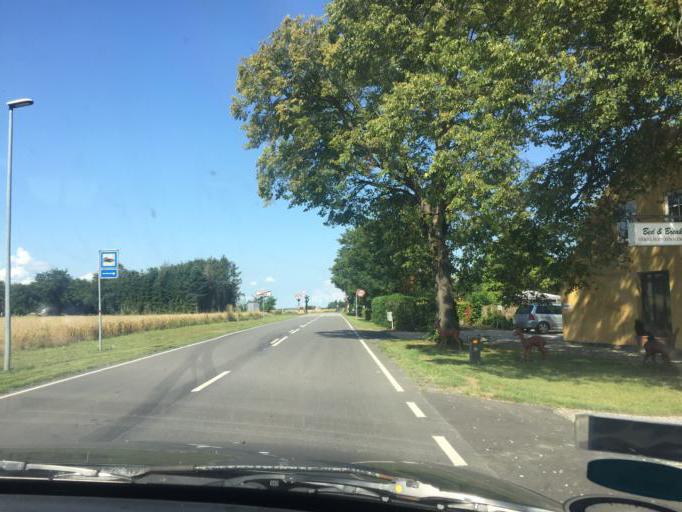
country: DK
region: Zealand
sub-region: Guldborgsund Kommune
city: Sakskobing
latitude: 54.7925
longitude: 11.5737
